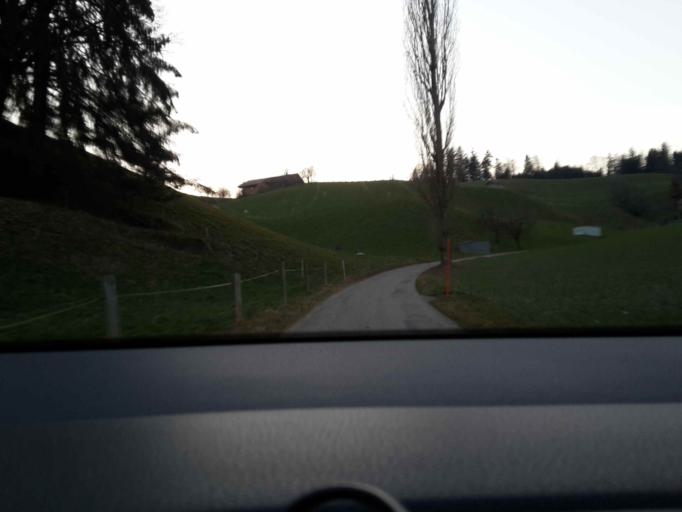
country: CH
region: Bern
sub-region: Oberaargau
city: Rohrbach
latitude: 47.1204
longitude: 7.7962
